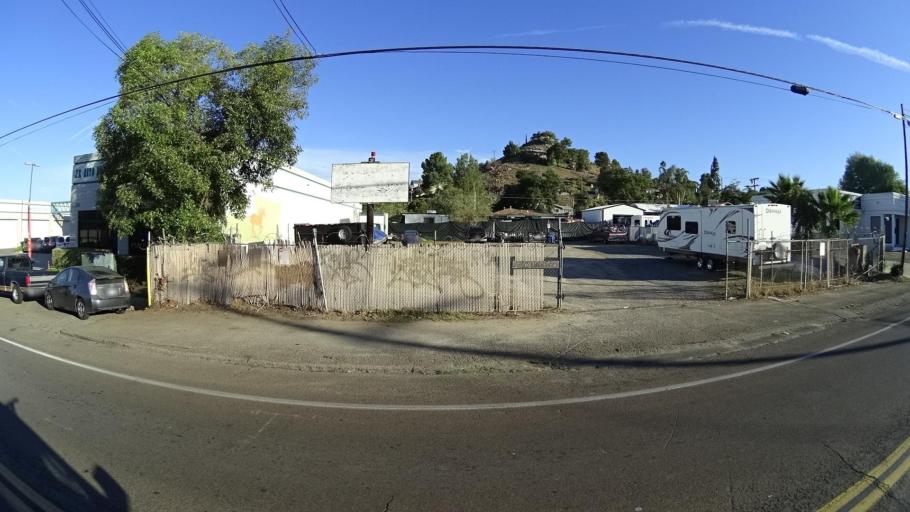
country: US
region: California
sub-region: San Diego County
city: Bostonia
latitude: 32.8134
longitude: -116.9432
